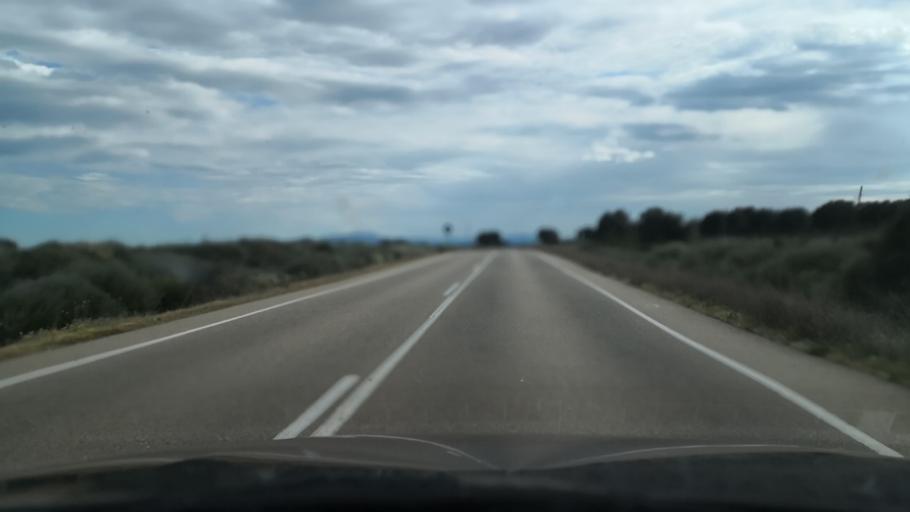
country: ES
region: Castille and Leon
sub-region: Provincia de Salamanca
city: Herguijuela de Ciudad Rodrigo
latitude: 40.4566
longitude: -6.5902
